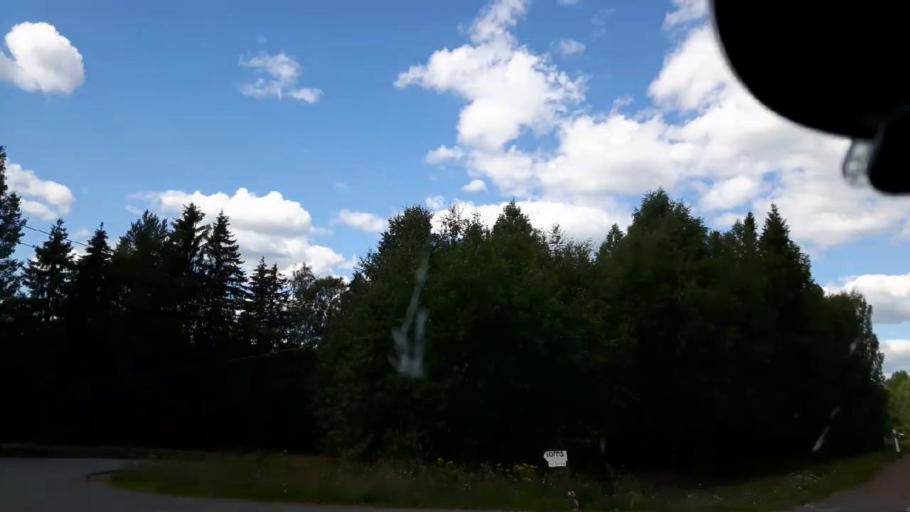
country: SE
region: Jaemtland
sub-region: Ragunda Kommun
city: Hammarstrand
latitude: 62.9281
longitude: 16.6981
